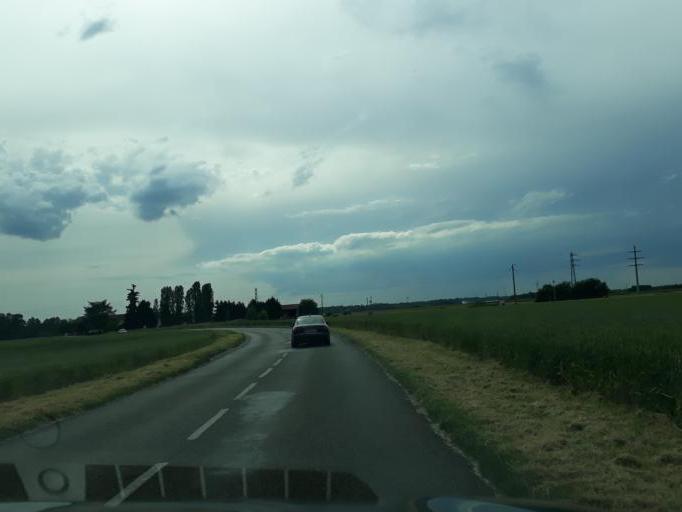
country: FR
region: Centre
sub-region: Departement du Loiret
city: Saint-Cyr-en-Val
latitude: 47.8365
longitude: 1.9921
